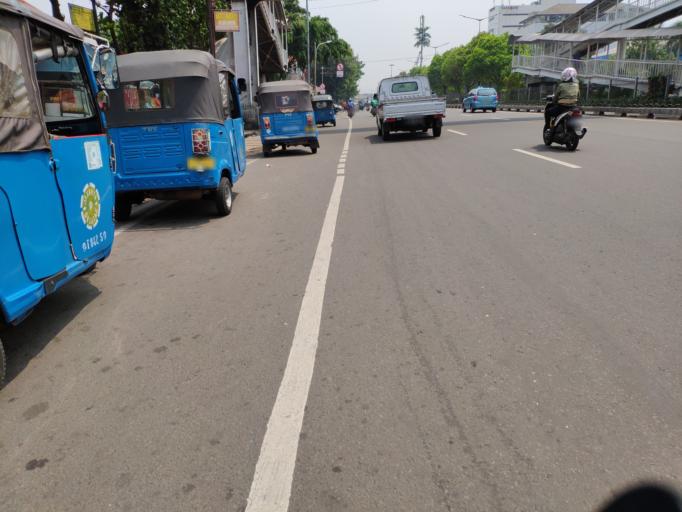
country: ID
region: Jakarta Raya
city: Jakarta
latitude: -6.2084
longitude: 106.8594
